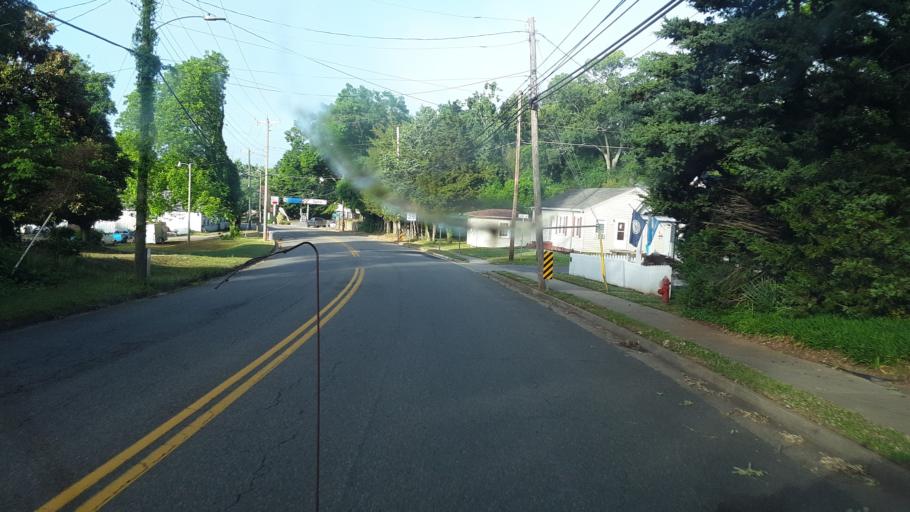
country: US
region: Virginia
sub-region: Pittsylvania County
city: Chatham
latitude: 36.8345
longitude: -79.3951
